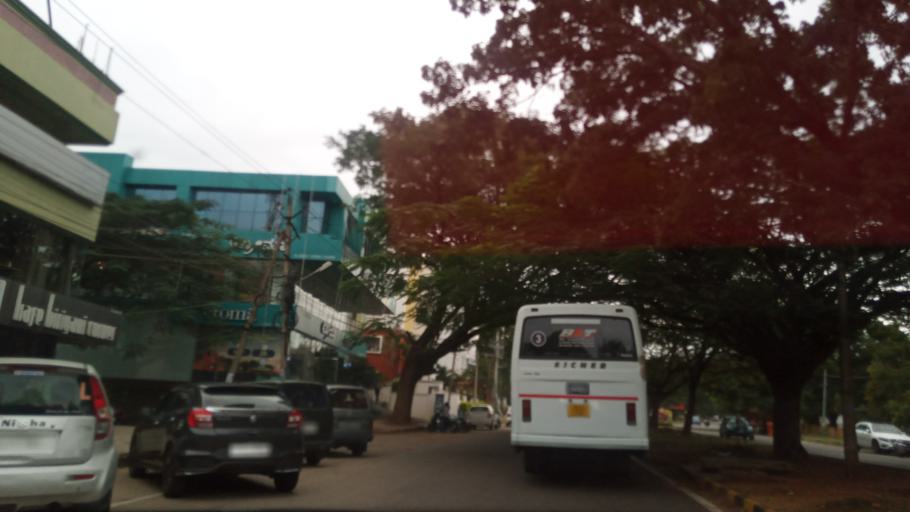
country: IN
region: Karnataka
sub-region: Mysore
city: Mysore
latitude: 12.2946
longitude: 76.6256
